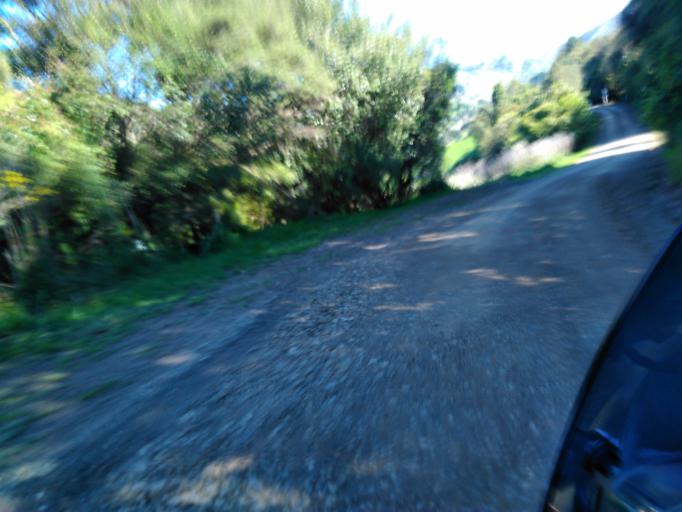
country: NZ
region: Gisborne
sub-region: Gisborne District
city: Gisborne
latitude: -38.3876
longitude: 177.6229
